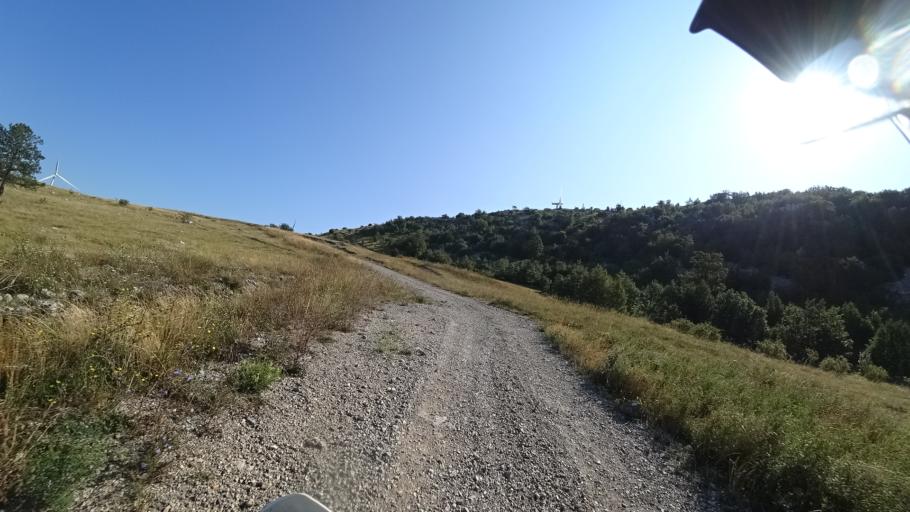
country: HR
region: Zadarska
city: Gracac
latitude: 44.2595
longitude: 16.0766
